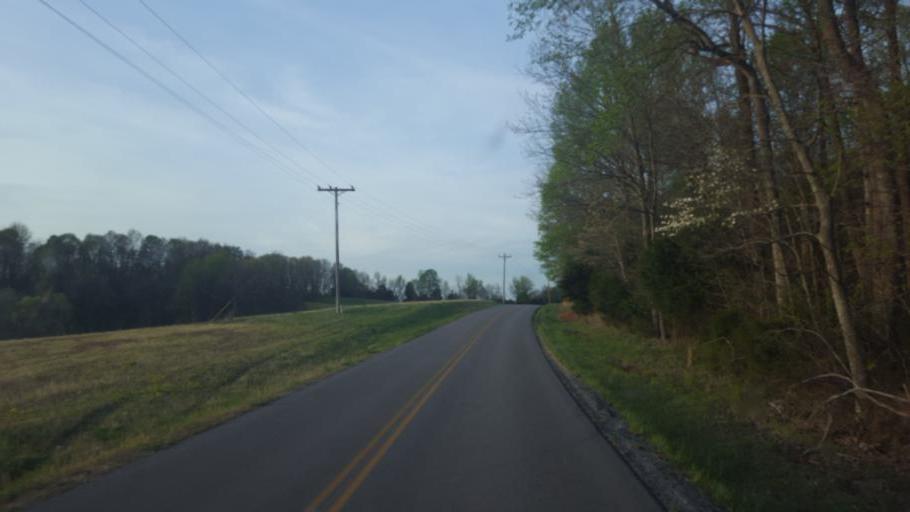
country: US
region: Kentucky
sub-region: Metcalfe County
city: Edmonton
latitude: 37.0295
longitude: -85.7186
